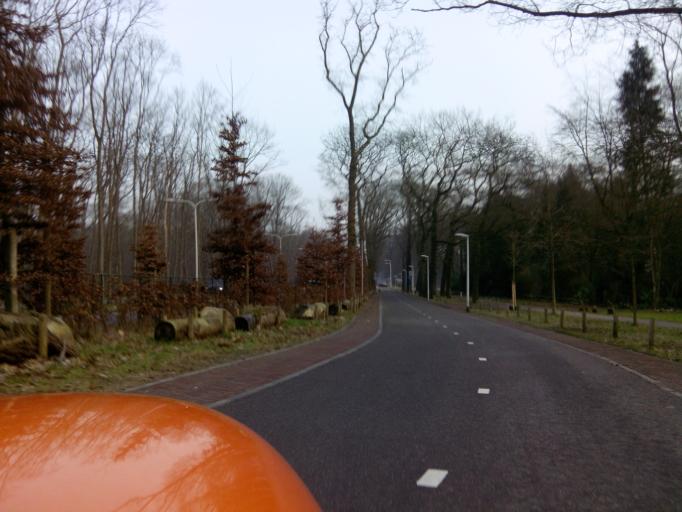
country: NL
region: Utrecht
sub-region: Gemeente Zeist
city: Zeist
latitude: 52.1018
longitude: 5.2646
